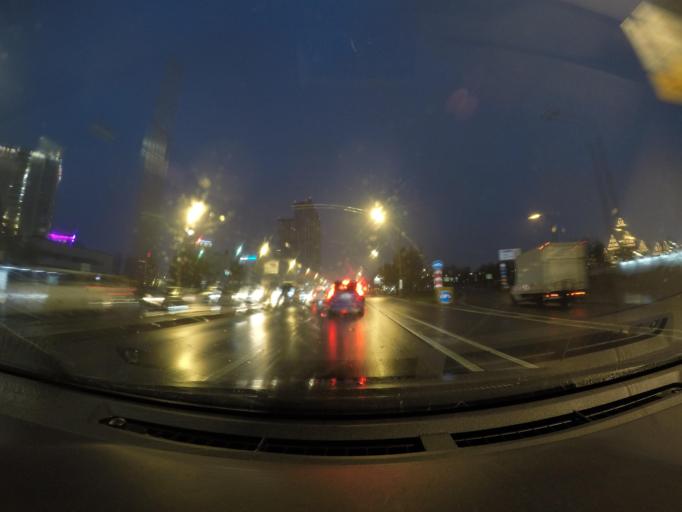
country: RU
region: Moskovskaya
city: Kozhukhovo
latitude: 55.6912
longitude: 37.6661
